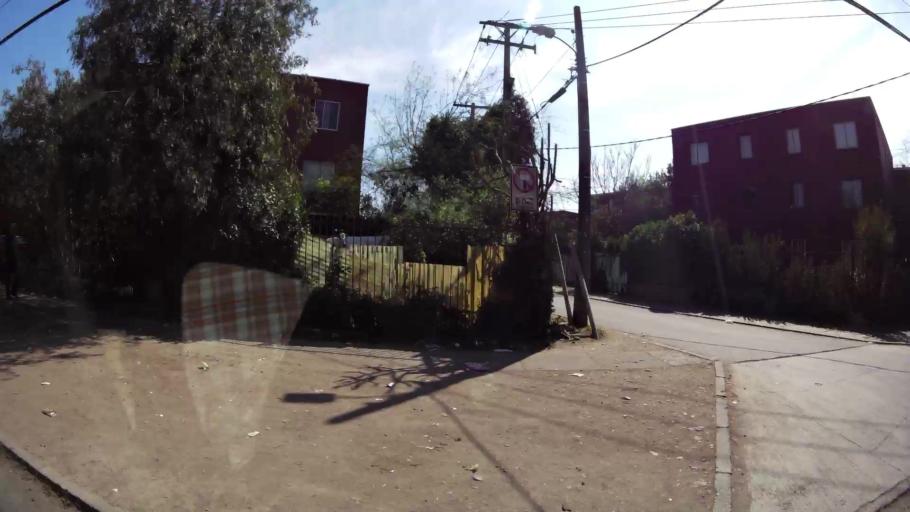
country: CL
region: Santiago Metropolitan
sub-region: Provincia de Santiago
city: Santiago
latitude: -33.3977
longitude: -70.6561
